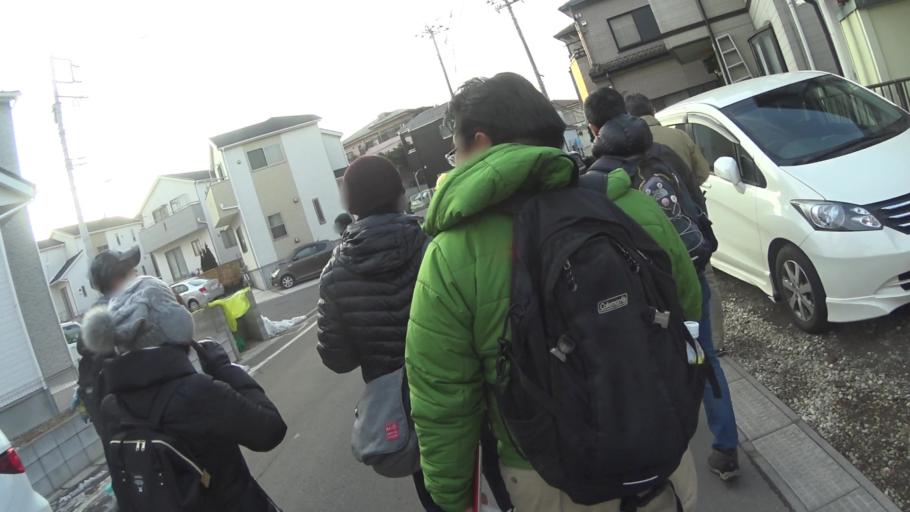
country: JP
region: Chiba
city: Funabashi
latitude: 35.7429
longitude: 140.0029
